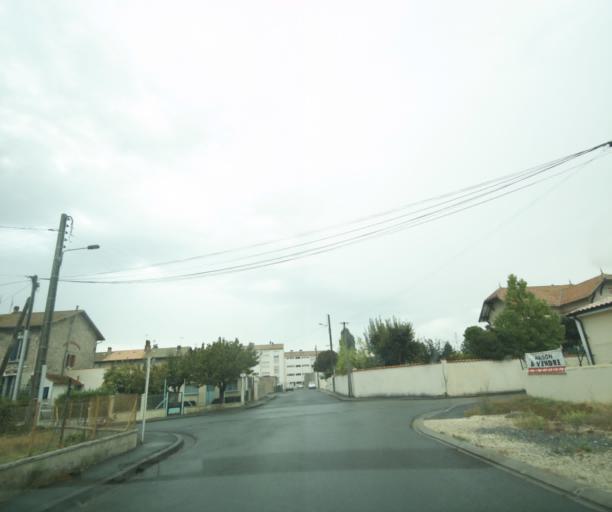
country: FR
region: Poitou-Charentes
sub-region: Departement de la Charente-Maritime
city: Tonnay-Charente
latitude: 45.9456
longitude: -0.9032
